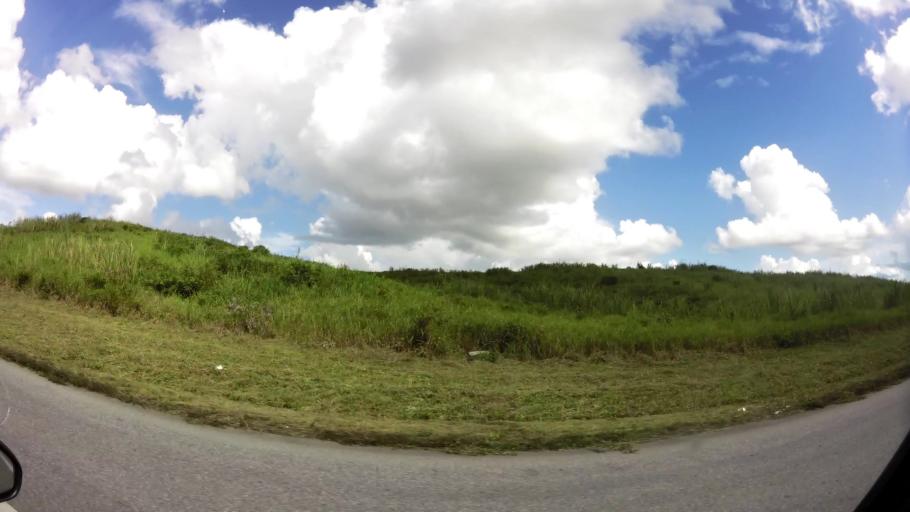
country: TT
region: Penal/Debe
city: Debe
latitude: 10.2390
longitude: -61.4379
